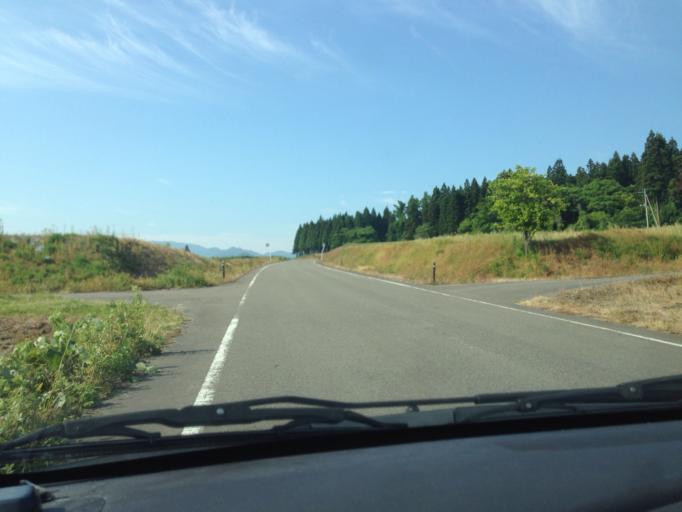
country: JP
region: Fukushima
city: Kitakata
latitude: 37.4743
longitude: 139.8139
